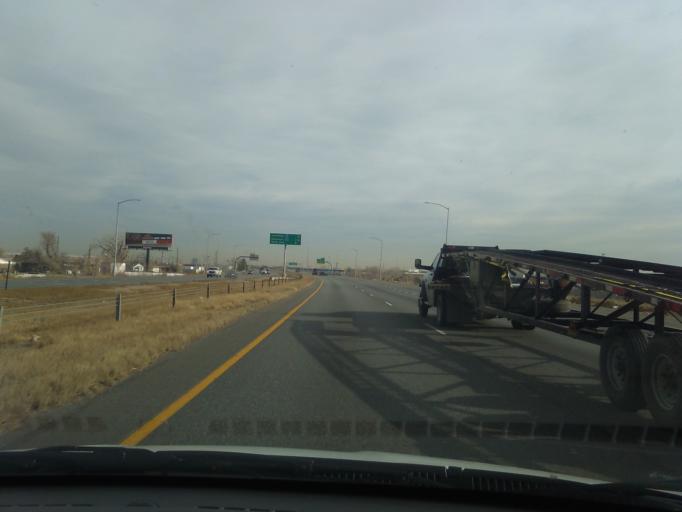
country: US
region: Colorado
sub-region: Adams County
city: Twin Lakes
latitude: 39.8110
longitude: -104.9966
